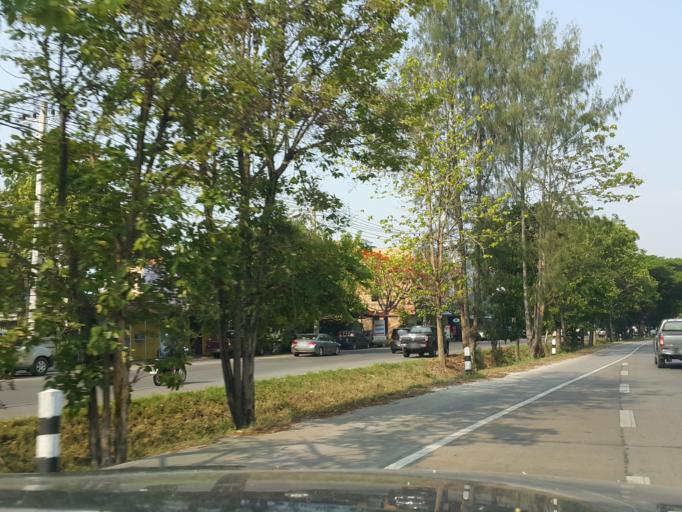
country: TH
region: Lampang
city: Lampang
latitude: 18.2810
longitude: 99.4907
